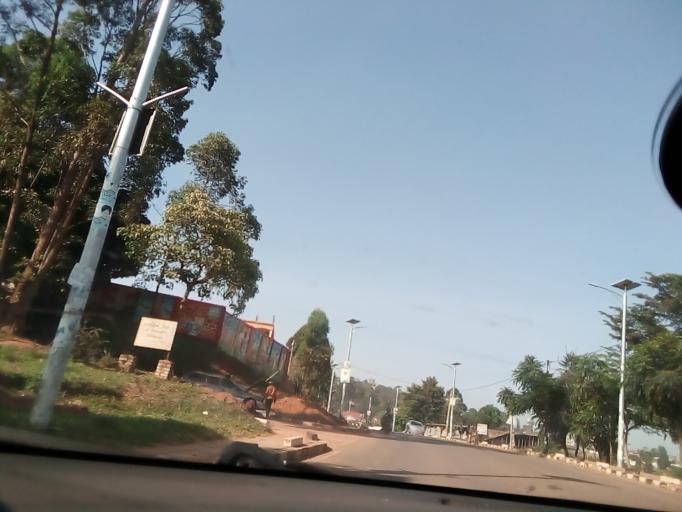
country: UG
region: Central Region
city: Masaka
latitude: -0.3236
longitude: 31.7383
